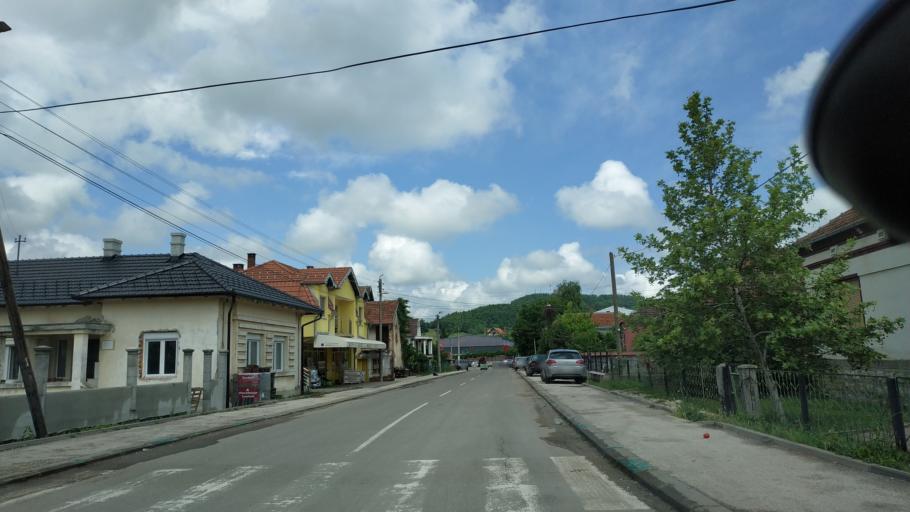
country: RS
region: Central Serbia
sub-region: Zajecarski Okrug
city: Boljevac
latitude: 43.8322
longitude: 21.9596
